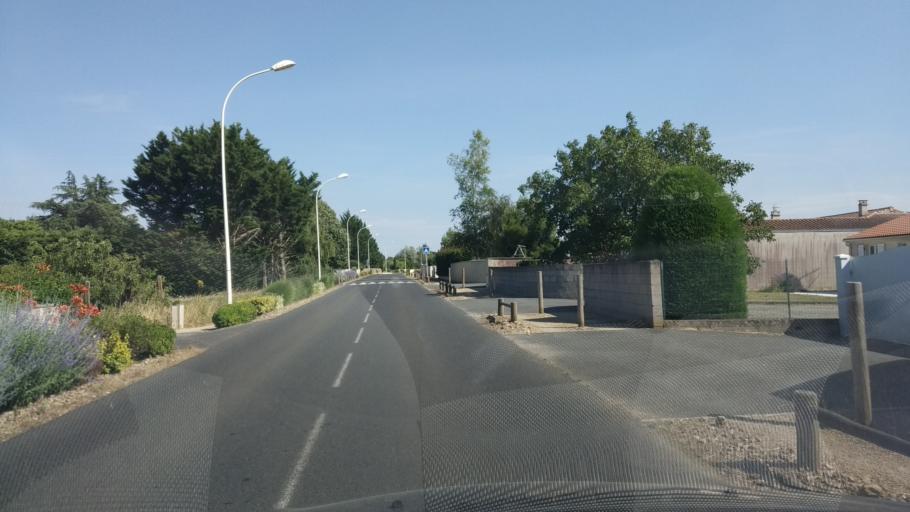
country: FR
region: Poitou-Charentes
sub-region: Departement de la Vienne
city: Cisse
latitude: 46.6417
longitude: 0.2360
